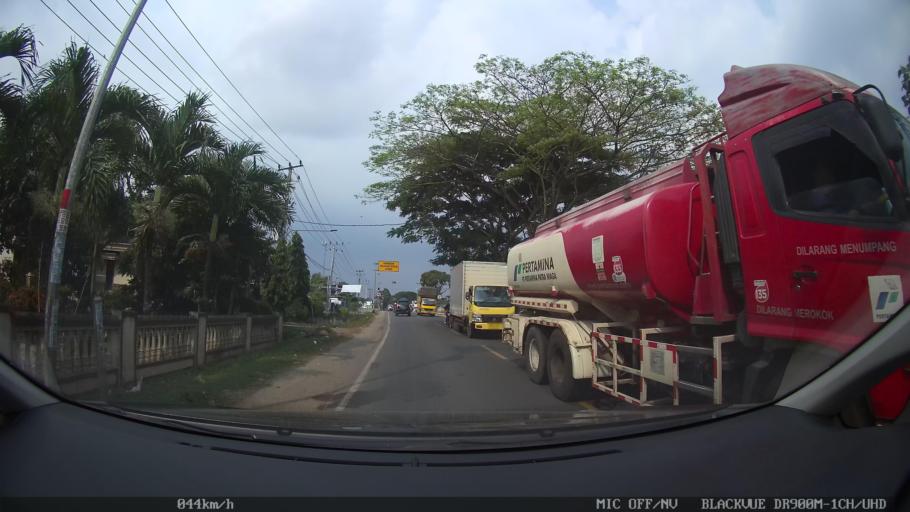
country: ID
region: Lampung
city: Gadingrejo
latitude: -5.3801
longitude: 105.0287
